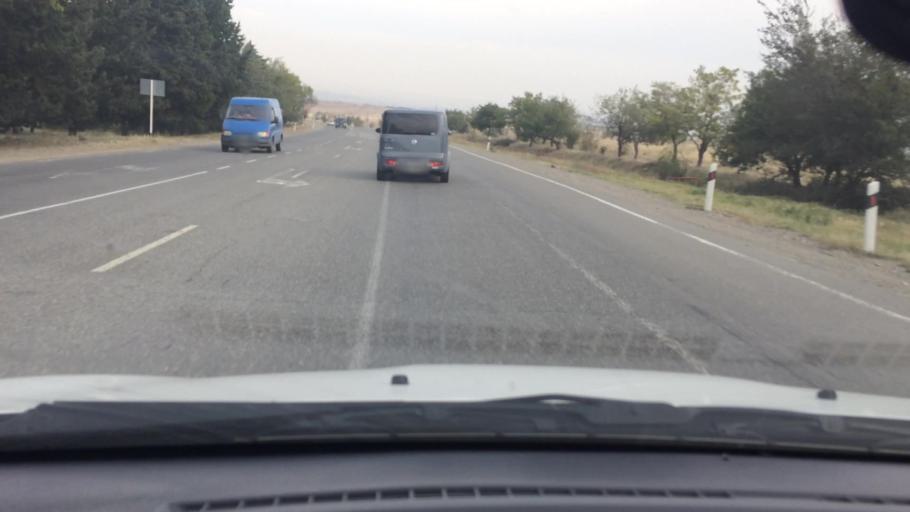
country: GE
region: T'bilisi
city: Tbilisi
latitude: 41.6393
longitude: 44.8690
